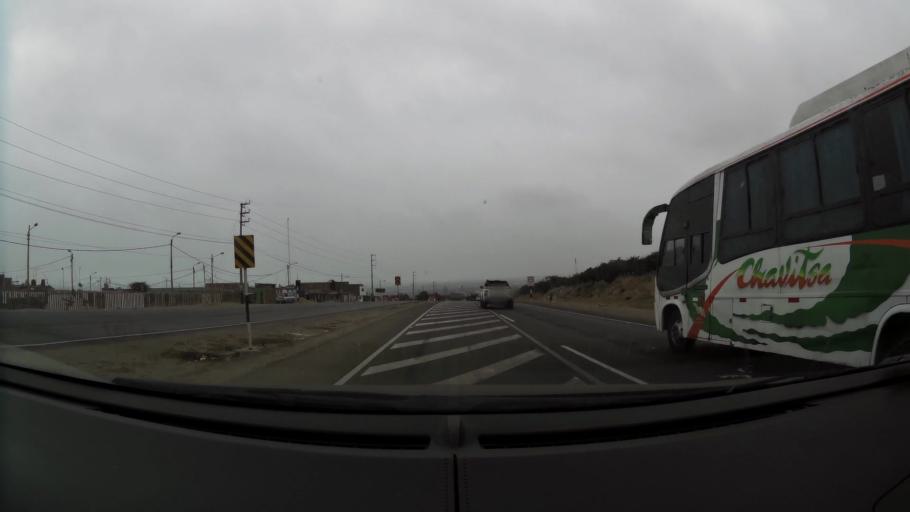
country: PE
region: La Libertad
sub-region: Provincia de Trujillo
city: Moche
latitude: -8.1869
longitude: -78.9813
